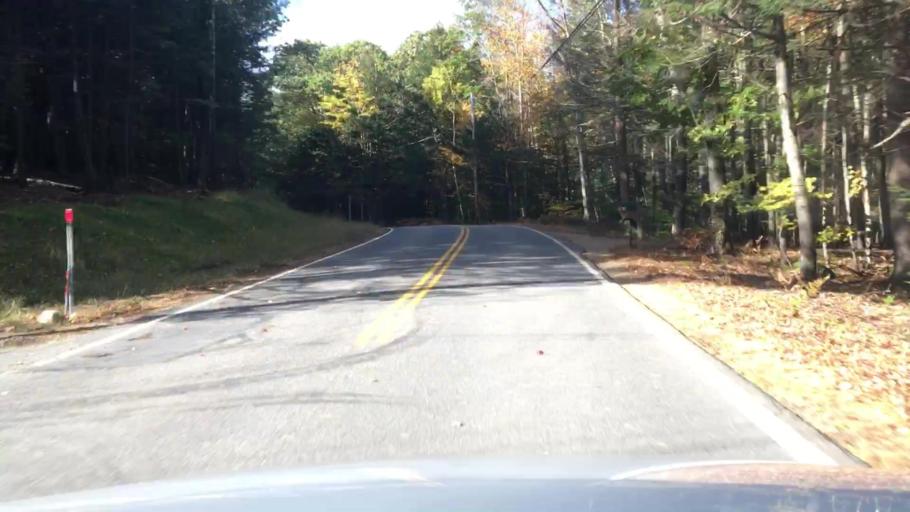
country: US
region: New Hampshire
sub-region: Strafford County
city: Barrington
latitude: 43.1792
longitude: -71.0396
